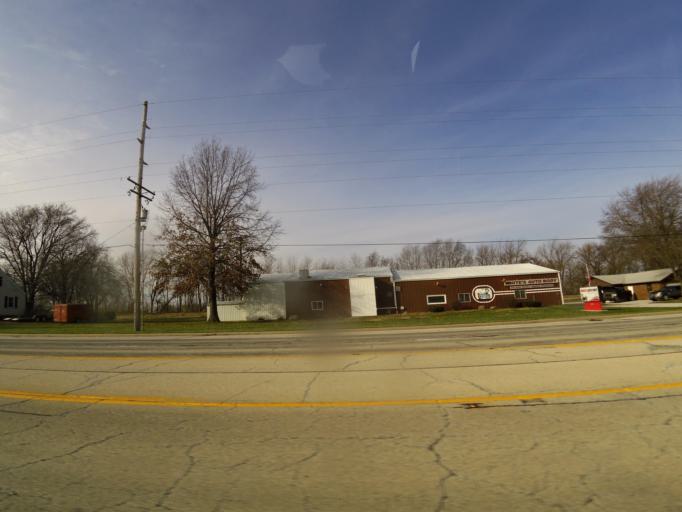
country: US
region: Illinois
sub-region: Macon County
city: Macon
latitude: 39.7764
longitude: -88.9800
